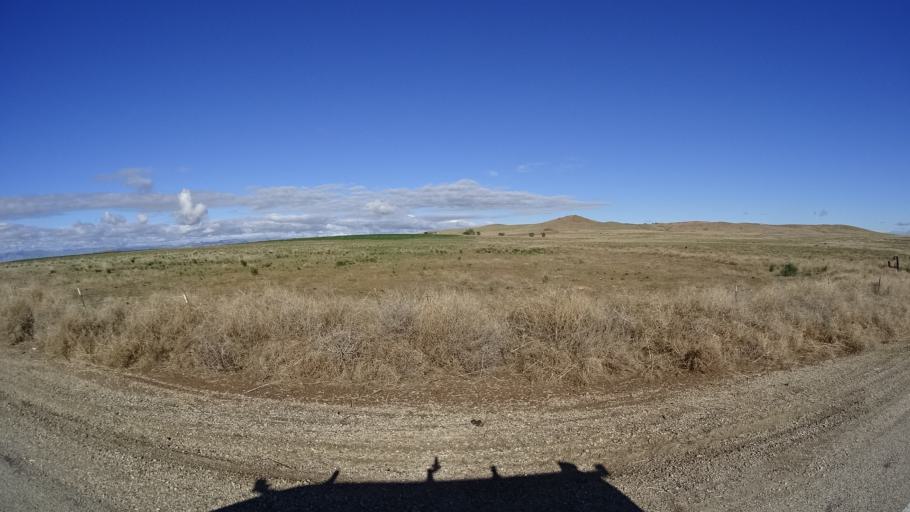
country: US
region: Idaho
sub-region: Ada County
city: Kuna
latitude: 43.4296
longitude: -116.4139
